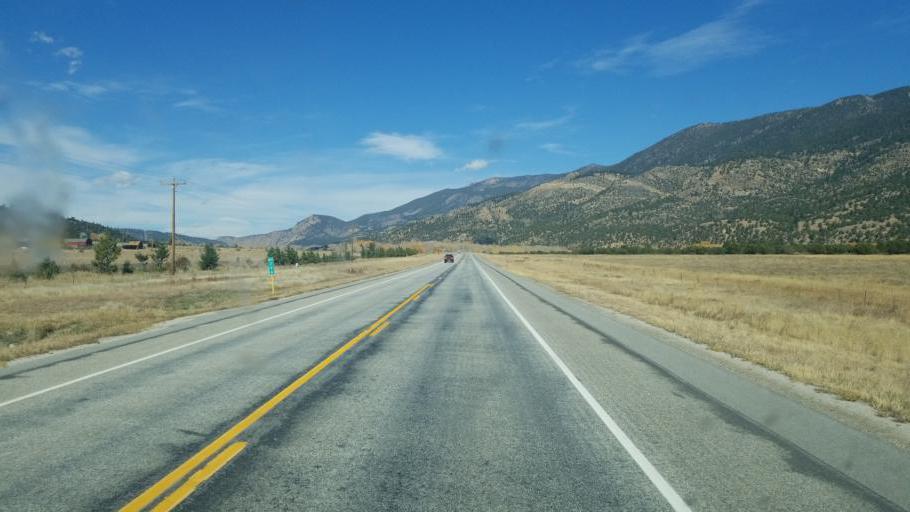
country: US
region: Colorado
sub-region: Chaffee County
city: Buena Vista
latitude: 38.9260
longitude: -106.1826
